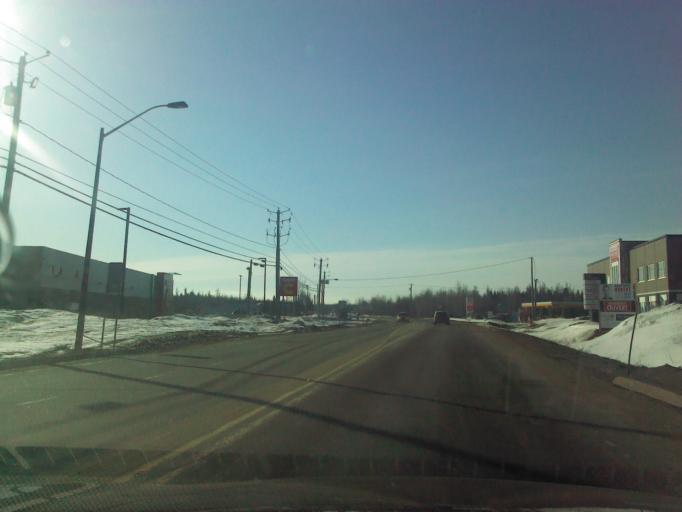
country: CA
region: Quebec
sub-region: Capitale-Nationale
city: Sainte Catherine de la Jacques Cartier
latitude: 46.8395
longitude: -71.6092
